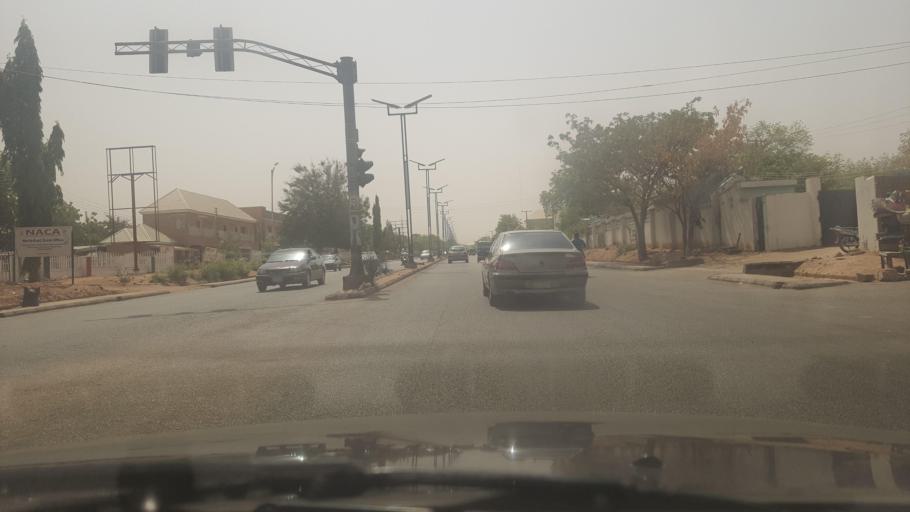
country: NG
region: Gombe
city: Gombe
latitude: 10.2849
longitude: 11.1469
